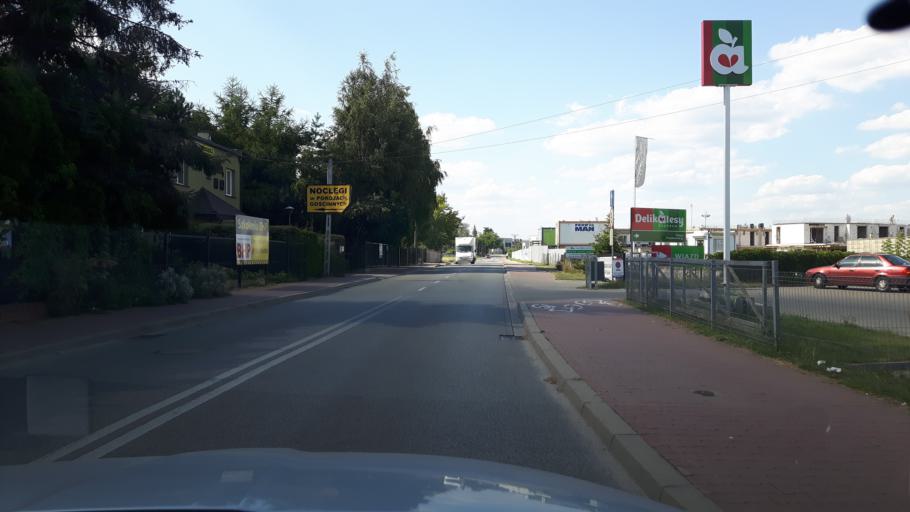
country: PL
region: Masovian Voivodeship
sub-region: Powiat pruszkowski
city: Nowe Grocholice
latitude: 52.1611
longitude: 20.9143
